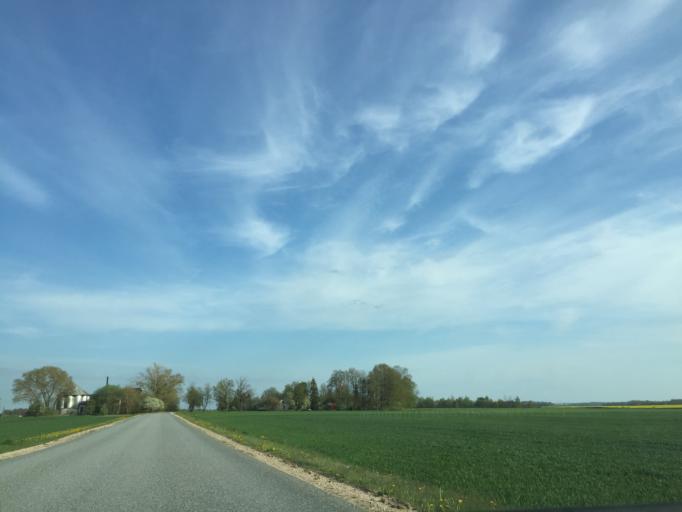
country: LV
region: Bauskas Rajons
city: Bauska
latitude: 56.3762
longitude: 24.2200
